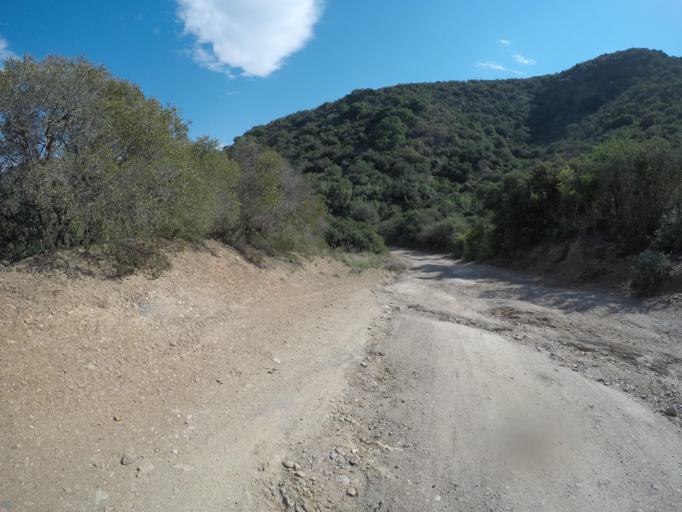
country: ZA
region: Eastern Cape
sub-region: Cacadu District Municipality
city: Kareedouw
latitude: -33.6546
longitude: 24.4032
